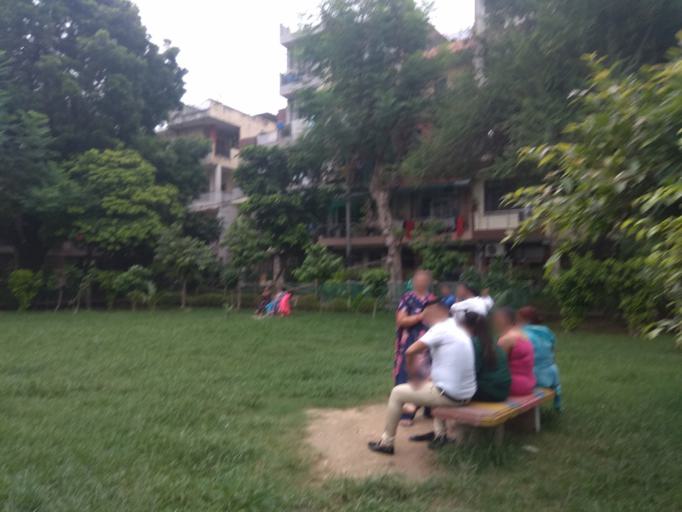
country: IN
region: NCT
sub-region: New Delhi
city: New Delhi
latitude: 28.5704
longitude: 77.2522
